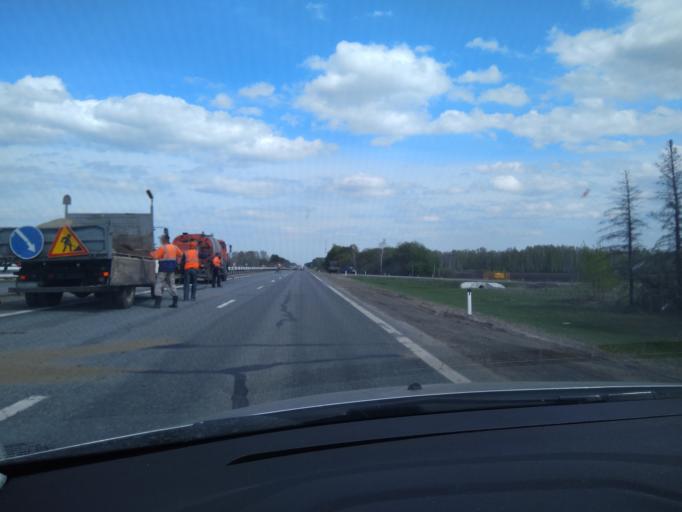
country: RU
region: Tjumen
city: Moskovskiy
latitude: 57.0955
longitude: 65.2074
